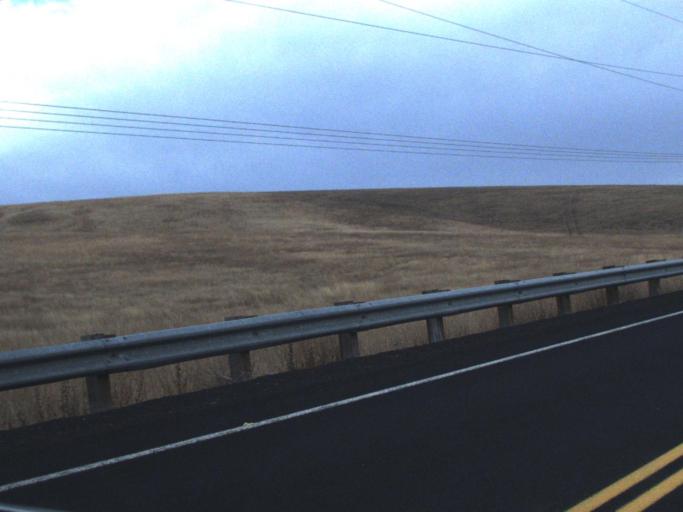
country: US
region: Washington
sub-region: Lincoln County
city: Davenport
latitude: 47.8582
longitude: -118.2145
